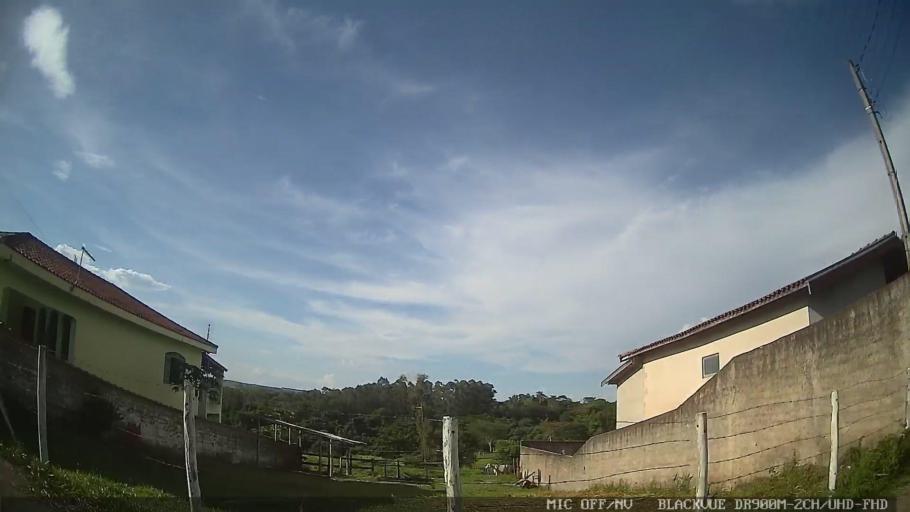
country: BR
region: Sao Paulo
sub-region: Tiete
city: Tiete
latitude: -23.0944
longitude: -47.7067
